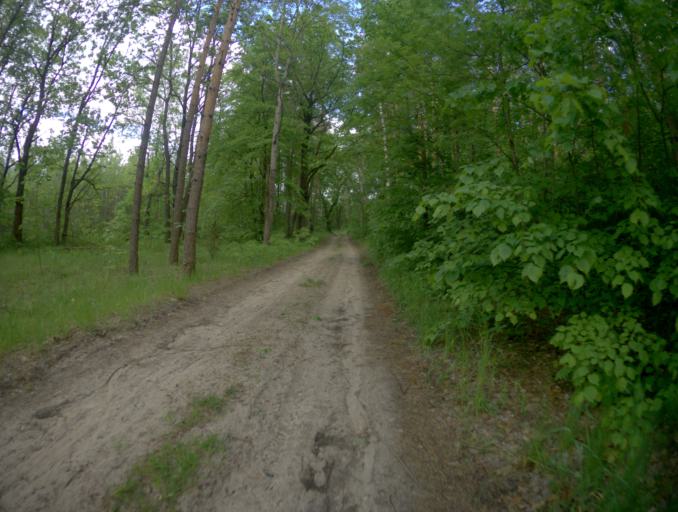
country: RU
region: Vladimir
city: Kommunar
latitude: 56.1108
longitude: 40.4912
